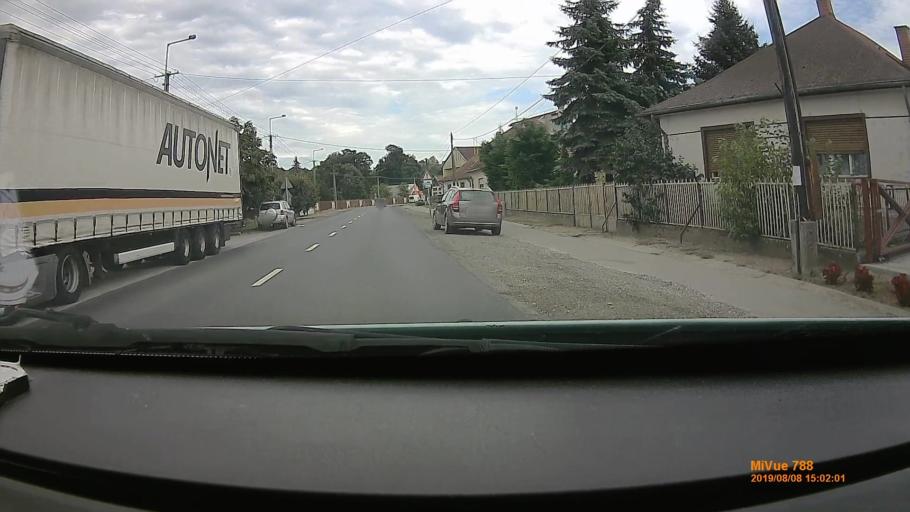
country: HU
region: Szabolcs-Szatmar-Bereg
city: Kocsord
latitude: 47.9396
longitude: 22.3930
